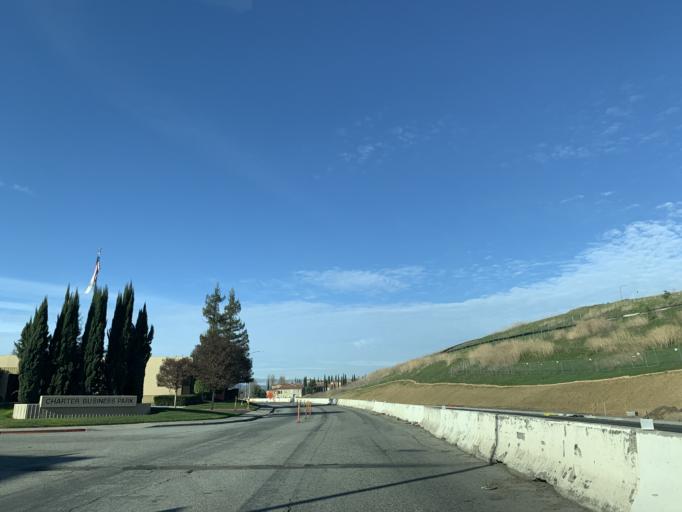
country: US
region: California
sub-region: Santa Clara County
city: Seven Trees
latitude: 37.2805
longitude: -121.8489
